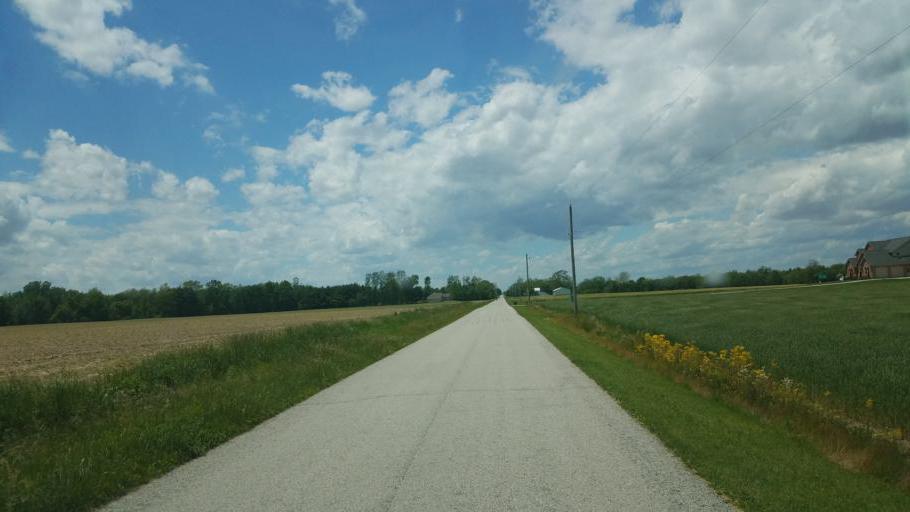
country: US
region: Ohio
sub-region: Huron County
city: Willard
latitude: 41.1427
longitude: -82.7729
